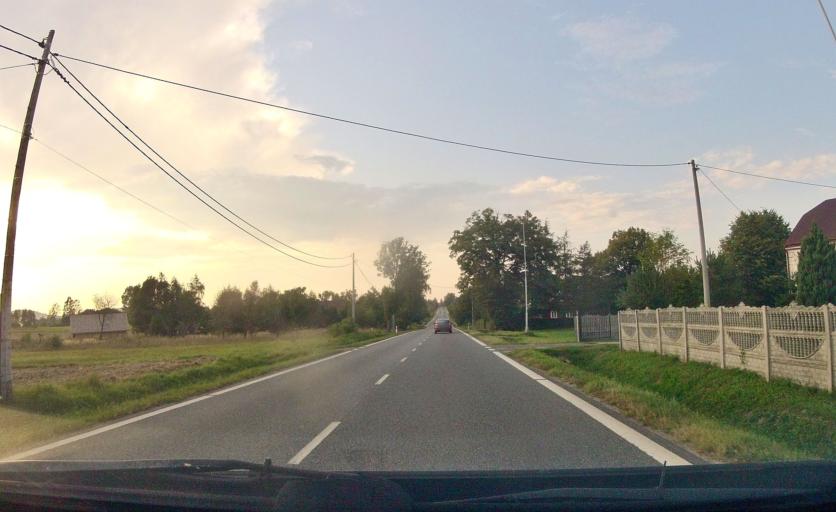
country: PL
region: Subcarpathian Voivodeship
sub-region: Powiat jasielski
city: Nowy Zmigrod
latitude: 49.5964
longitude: 21.5337
